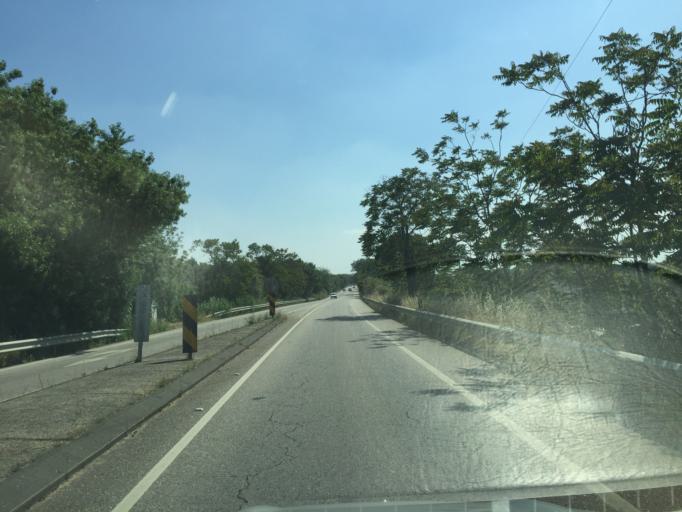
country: PT
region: Santarem
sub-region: Golega
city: Golega
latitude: 39.3919
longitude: -8.4413
